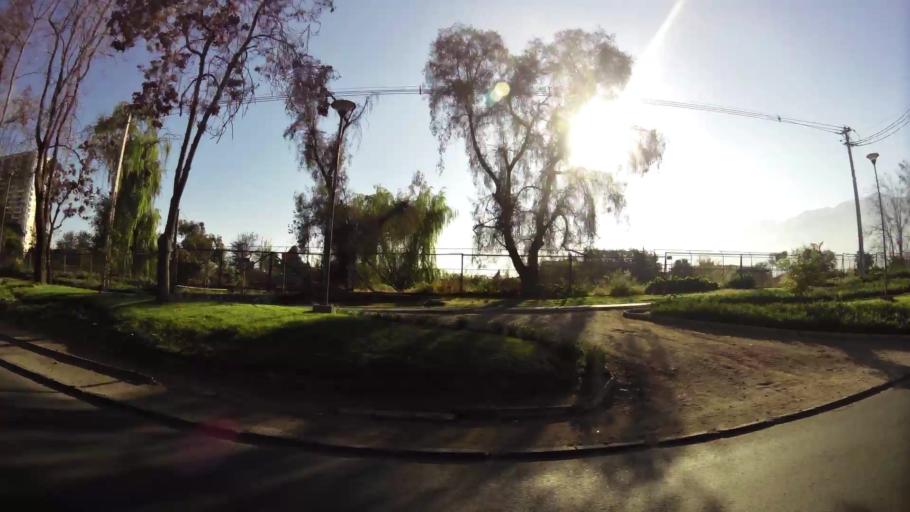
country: CL
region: Santiago Metropolitan
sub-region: Provincia de Santiago
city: Villa Presidente Frei, Nunoa, Santiago, Chile
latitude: -33.4408
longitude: -70.5708
